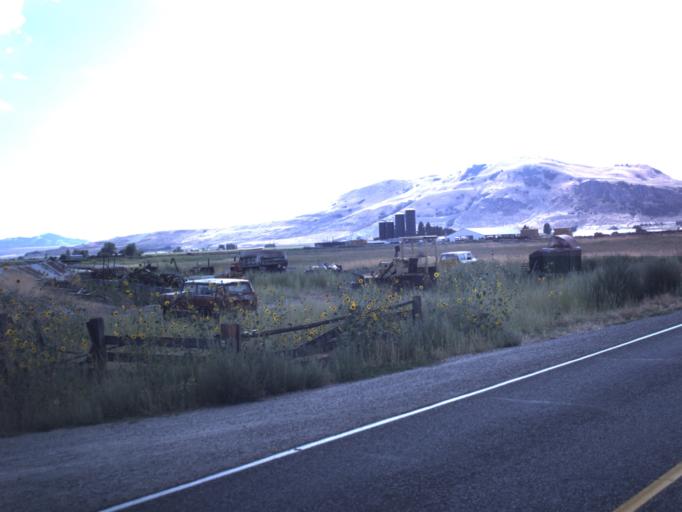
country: US
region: Utah
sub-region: Cache County
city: Lewiston
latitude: 41.9147
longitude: -111.9155
